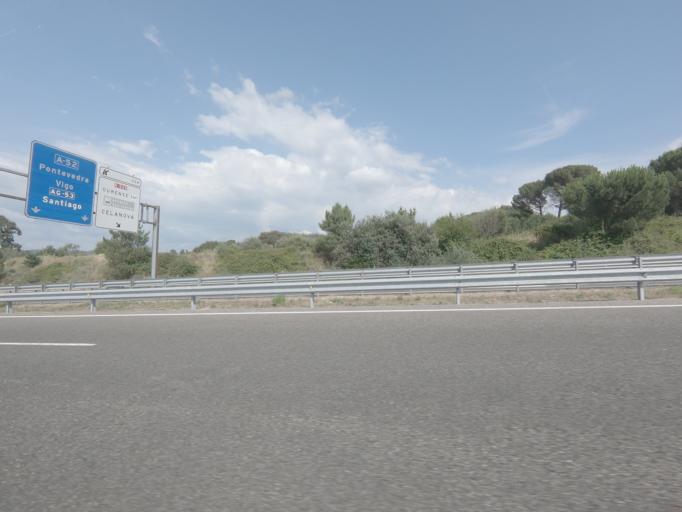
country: ES
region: Galicia
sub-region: Provincia de Ourense
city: Ourense
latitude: 42.3009
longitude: -7.8759
